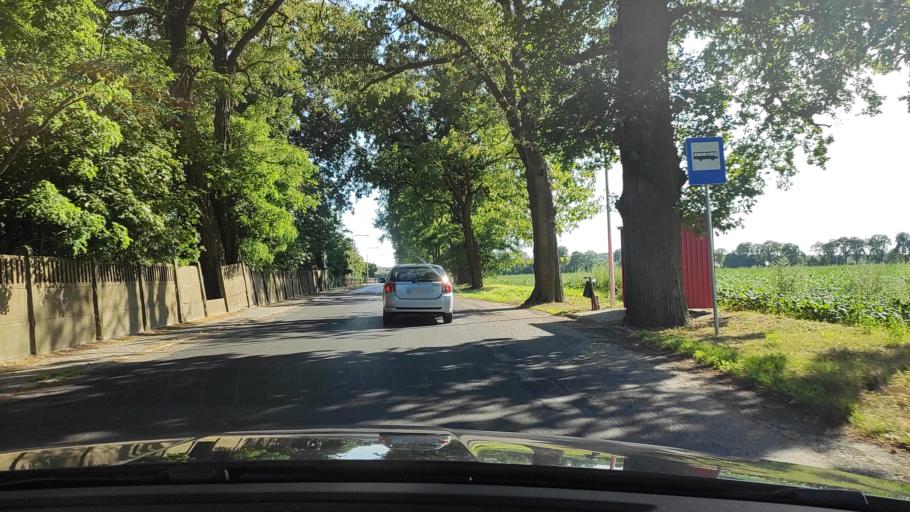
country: PL
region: Greater Poland Voivodeship
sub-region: Powiat poznanski
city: Kobylnica
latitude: 52.4945
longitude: 17.1009
